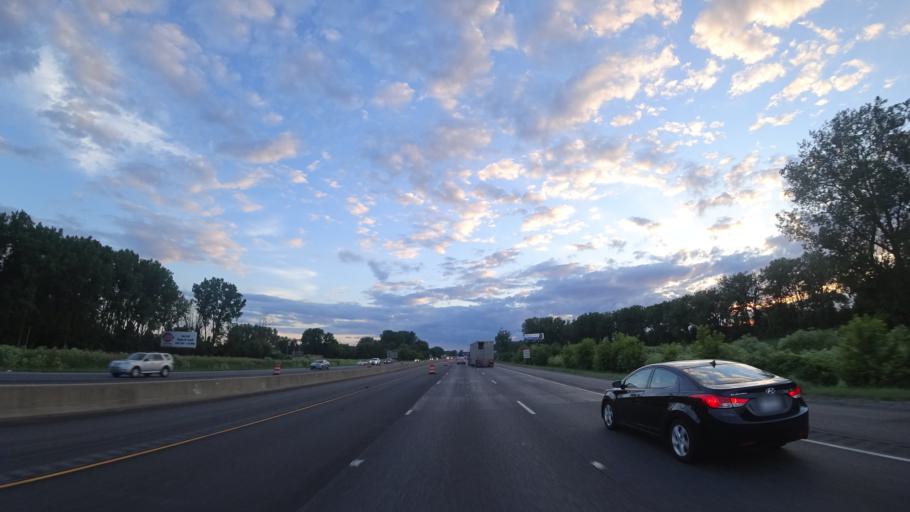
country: US
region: Indiana
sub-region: Porter County
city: Ogden Dunes
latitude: 41.5991
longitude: -87.1995
